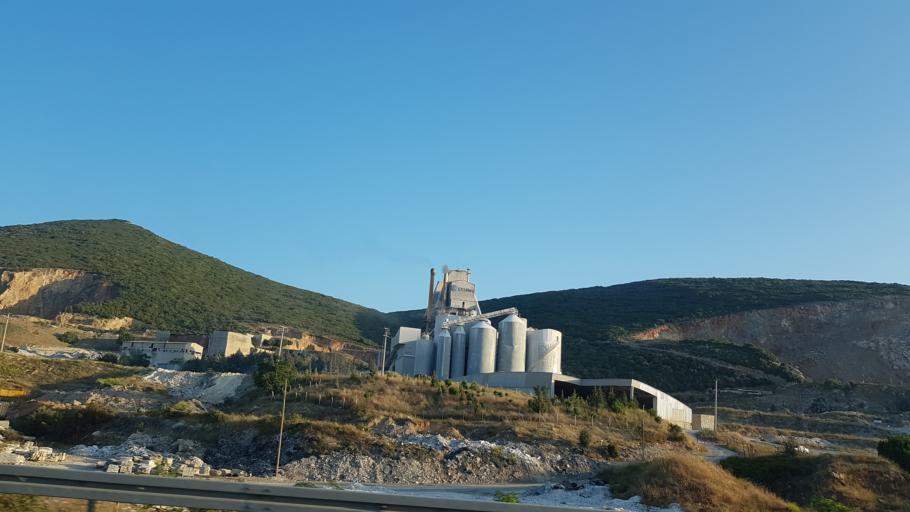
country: TR
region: Bursa
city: Umurbey
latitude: 40.4374
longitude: 29.2483
